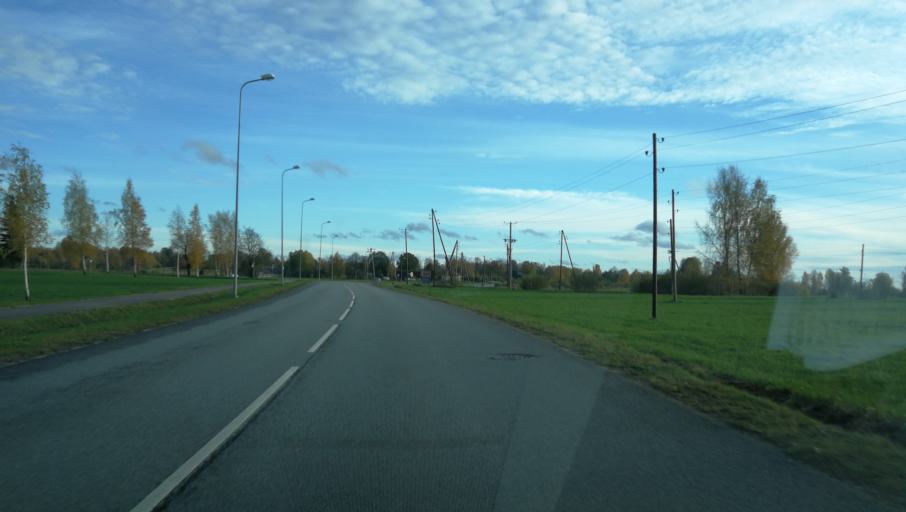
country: LV
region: Cesu Rajons
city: Cesis
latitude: 57.3022
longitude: 25.2433
